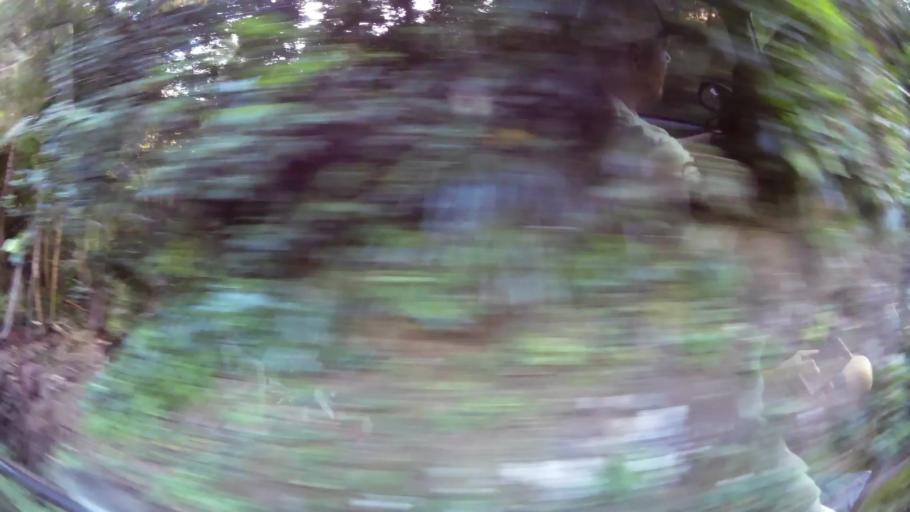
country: DM
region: Saint Andrew
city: Calibishie
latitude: 15.5923
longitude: -61.3900
